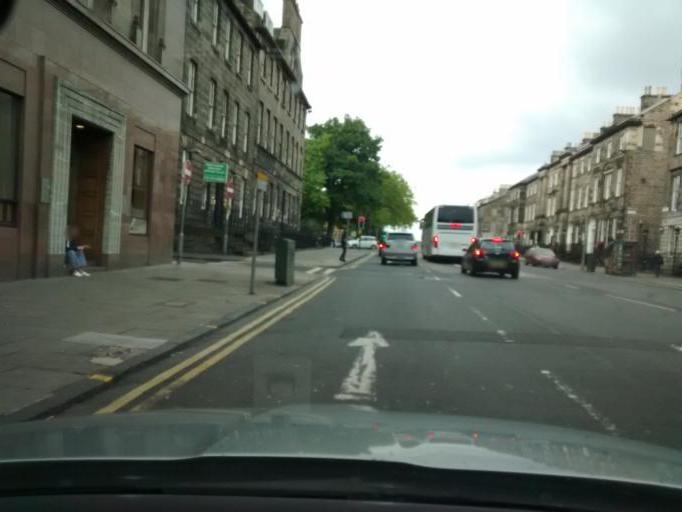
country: GB
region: Scotland
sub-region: Edinburgh
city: Edinburgh
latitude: 55.9506
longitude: -3.2061
